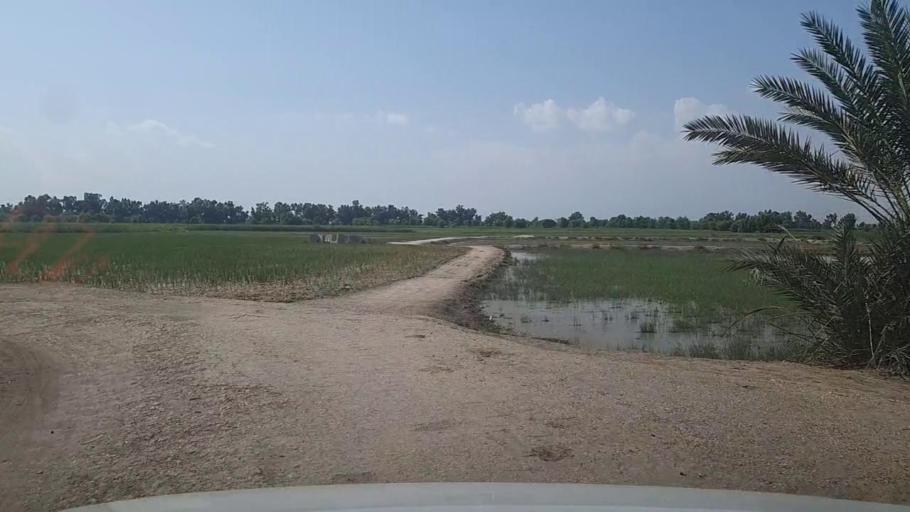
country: PK
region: Sindh
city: Khairpur
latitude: 28.1226
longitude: 69.6051
